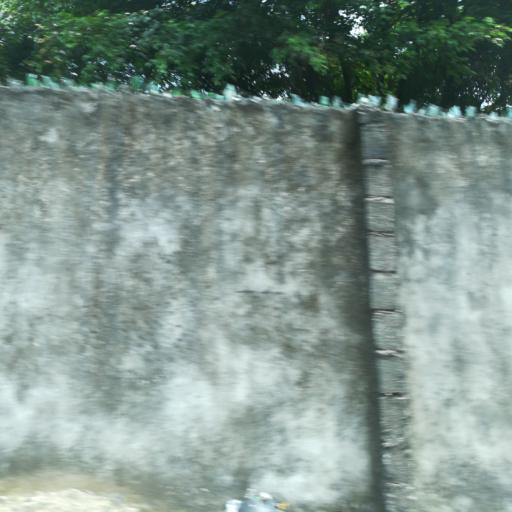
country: NG
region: Rivers
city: Port Harcourt
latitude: 4.7802
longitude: 7.0426
